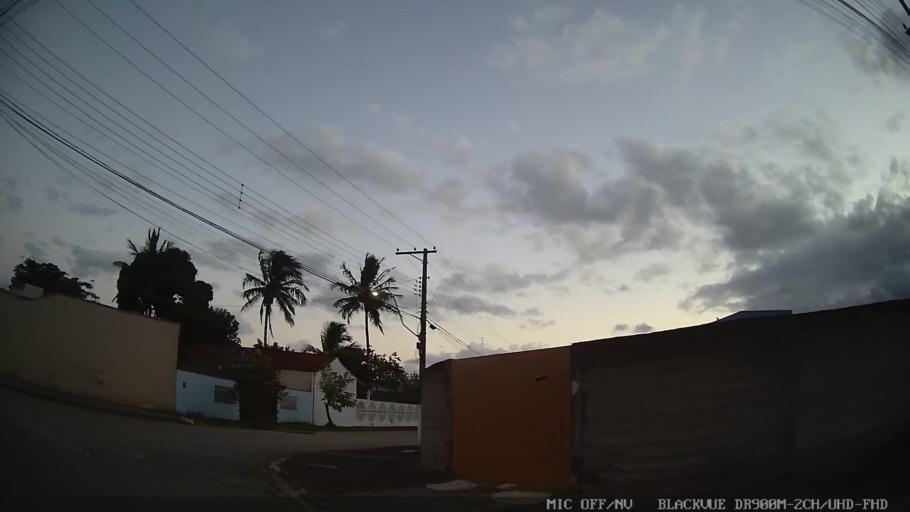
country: BR
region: Sao Paulo
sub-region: Caraguatatuba
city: Caraguatatuba
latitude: -23.6634
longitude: -45.4372
